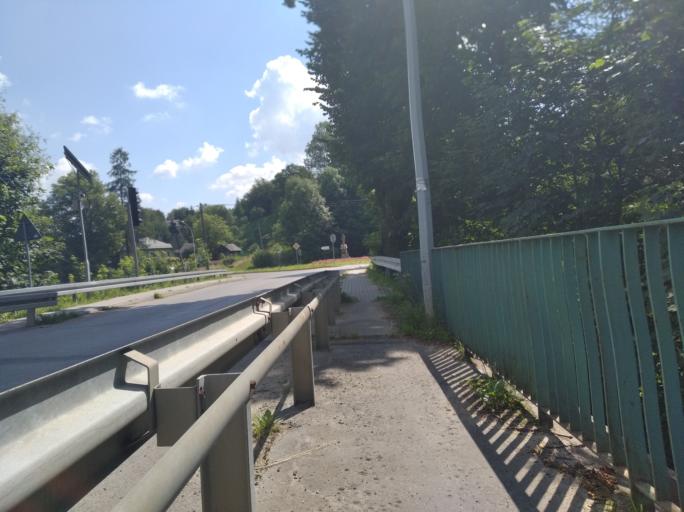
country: PL
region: Subcarpathian Voivodeship
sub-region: Powiat rzeszowski
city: Dynow
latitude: 49.8018
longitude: 22.2447
